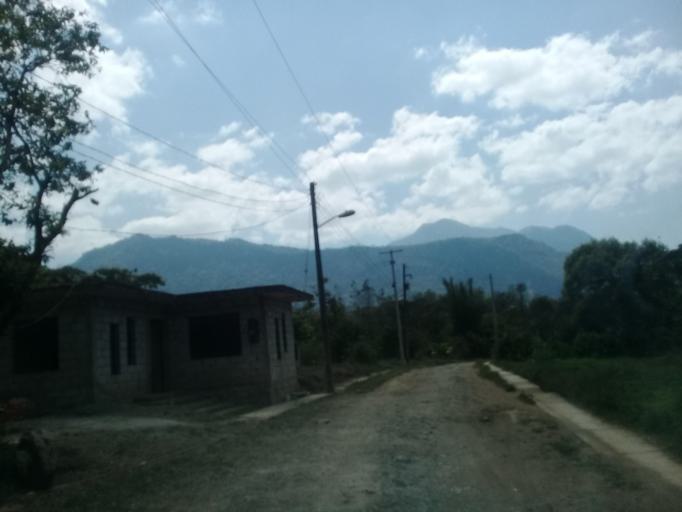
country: MX
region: Veracruz
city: Jalapilla
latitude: 18.8175
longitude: -97.0622
